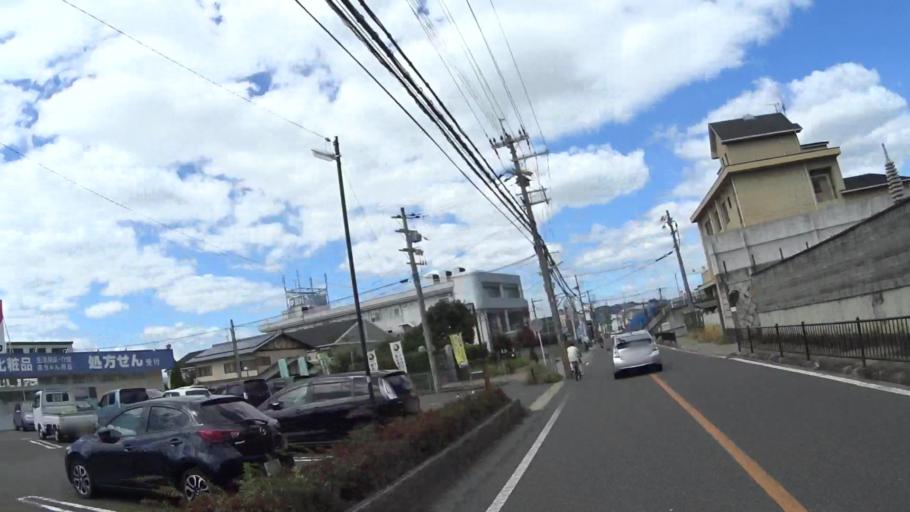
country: JP
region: Kyoto
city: Uji
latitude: 34.9191
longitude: 135.8004
